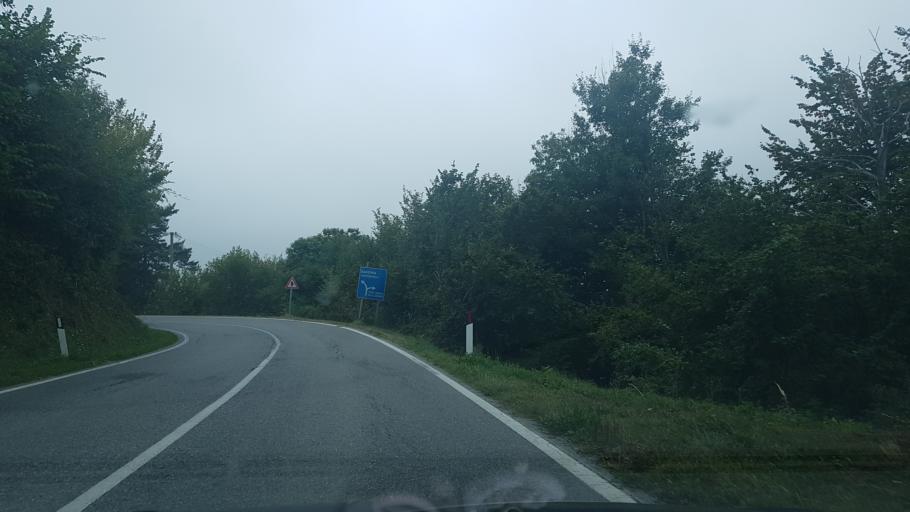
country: IT
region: Piedmont
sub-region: Provincia di Cuneo
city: Paroldo
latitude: 44.4181
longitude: 8.0904
